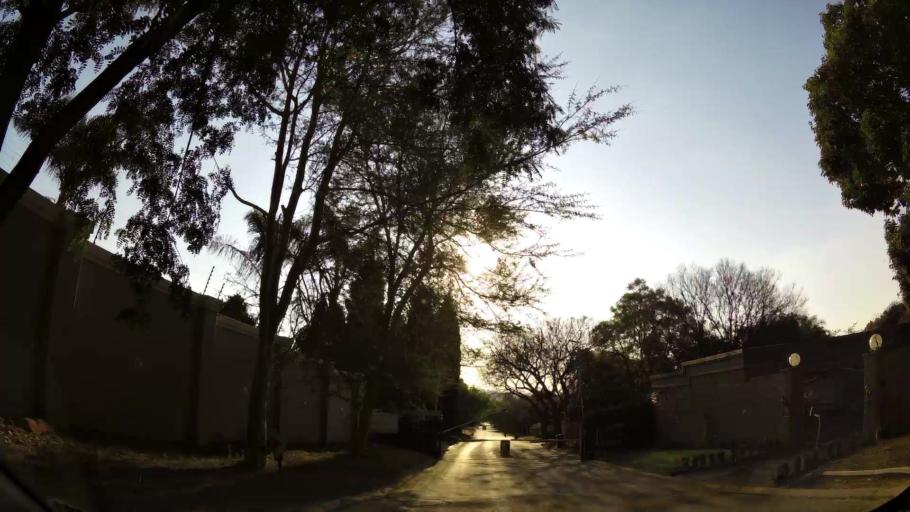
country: ZA
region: Gauteng
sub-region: City of Johannesburg Metropolitan Municipality
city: Diepsloot
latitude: -26.0612
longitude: 27.9917
